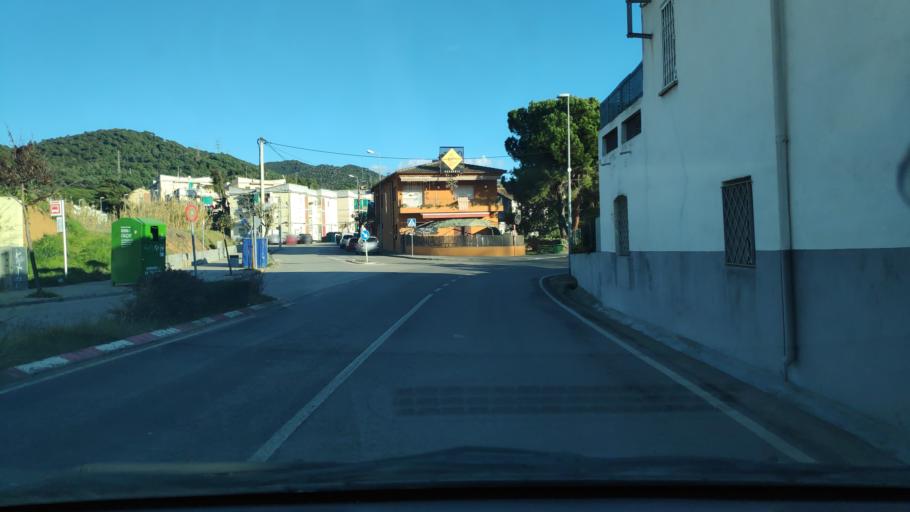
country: ES
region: Catalonia
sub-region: Provincia de Barcelona
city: Montmelo
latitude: 41.5277
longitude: 2.2409
